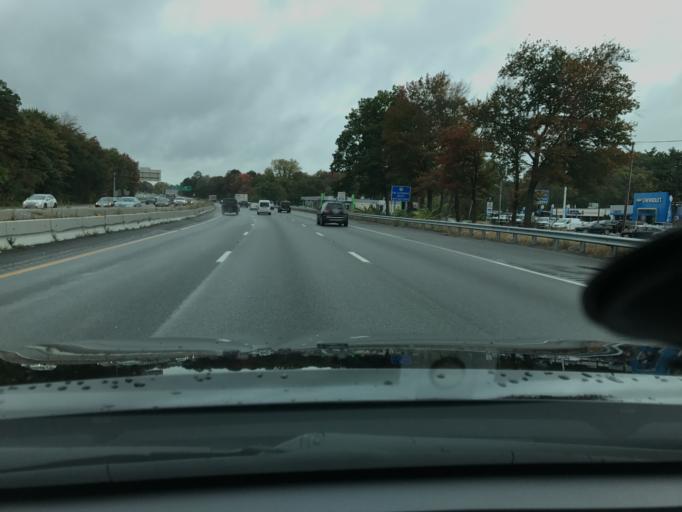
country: US
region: Massachusetts
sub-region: Middlesex County
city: Wakefield
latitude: 42.5270
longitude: -71.0714
